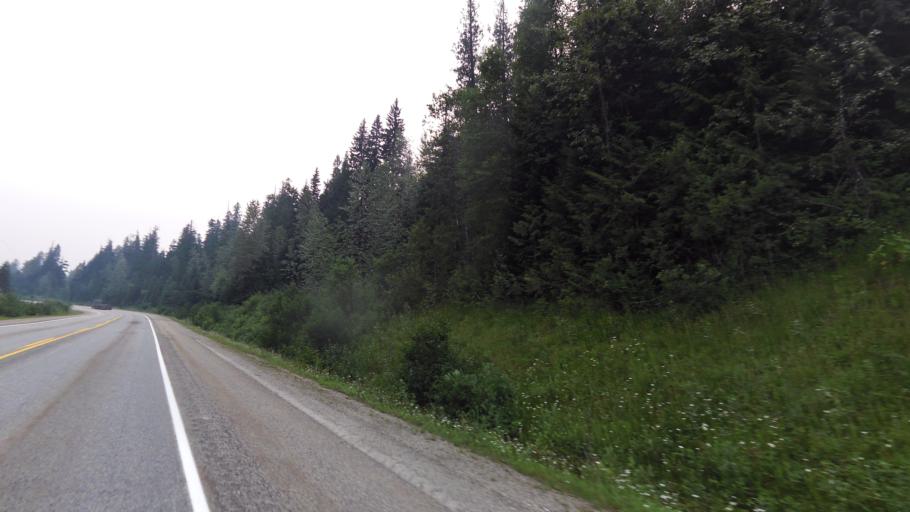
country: CA
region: Alberta
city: Jasper Park Lodge
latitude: 52.3346
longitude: -119.1781
